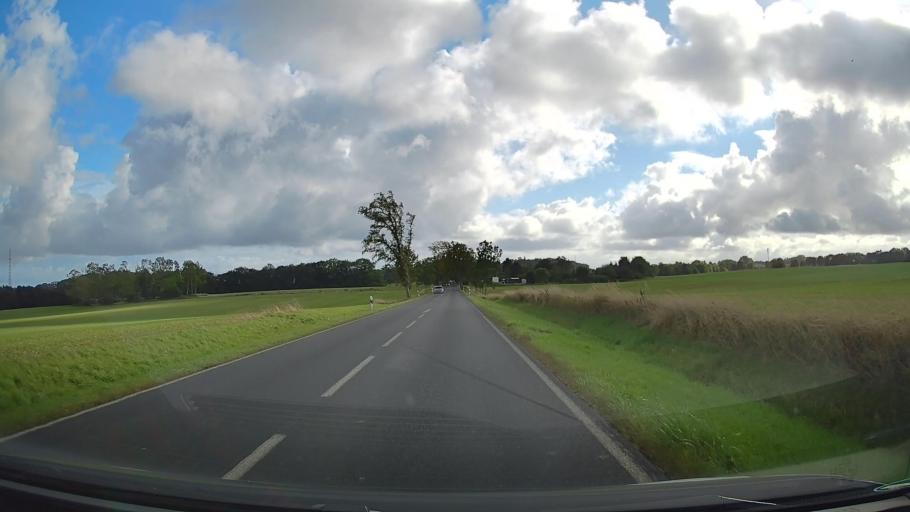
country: DE
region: Mecklenburg-Vorpommern
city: Putbus
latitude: 54.3668
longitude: 13.4784
